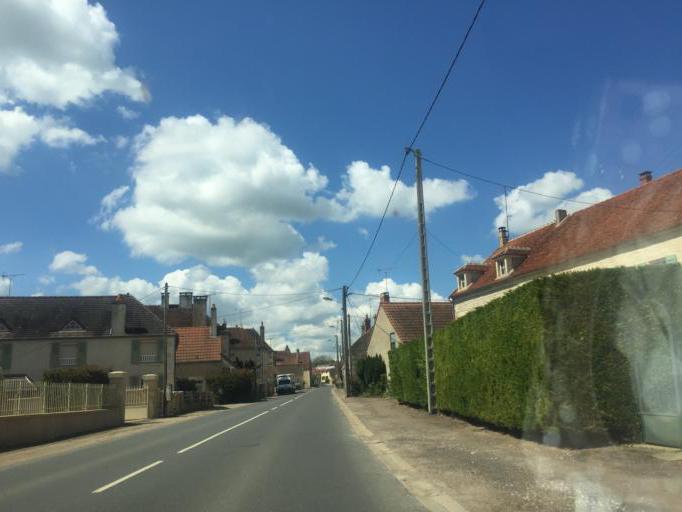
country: FR
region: Bourgogne
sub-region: Departement de l'Yonne
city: Fontenailles
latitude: 47.4804
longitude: 3.4174
